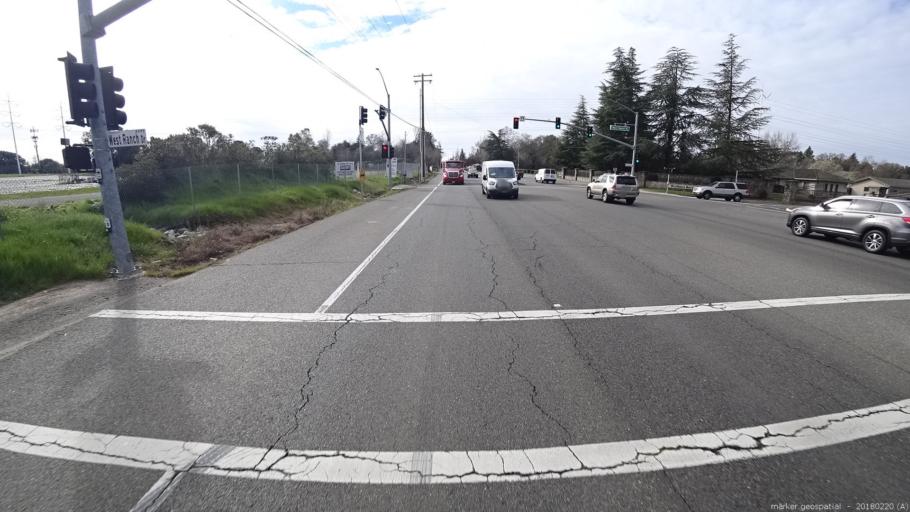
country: US
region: California
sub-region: Sacramento County
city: Orangevale
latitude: 38.7163
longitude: -121.2258
